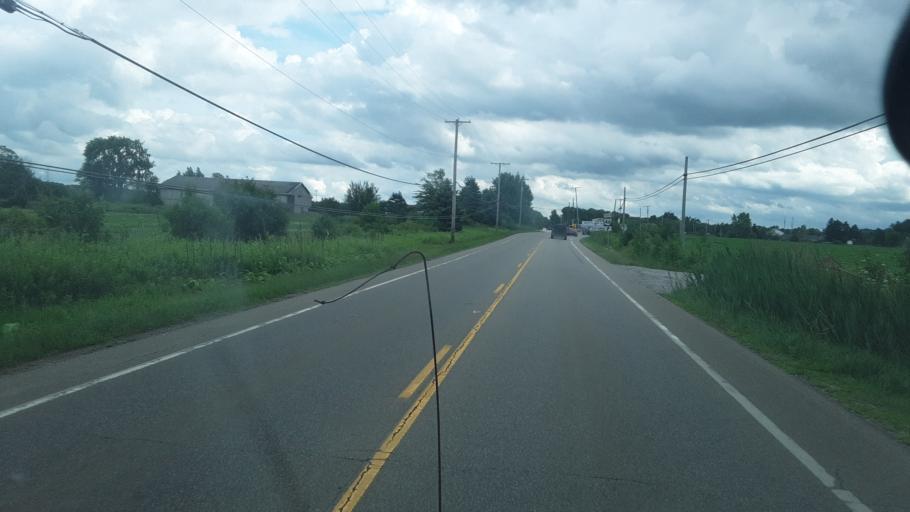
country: US
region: Ohio
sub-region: Ashtabula County
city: Jefferson
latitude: 41.7632
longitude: -80.7648
